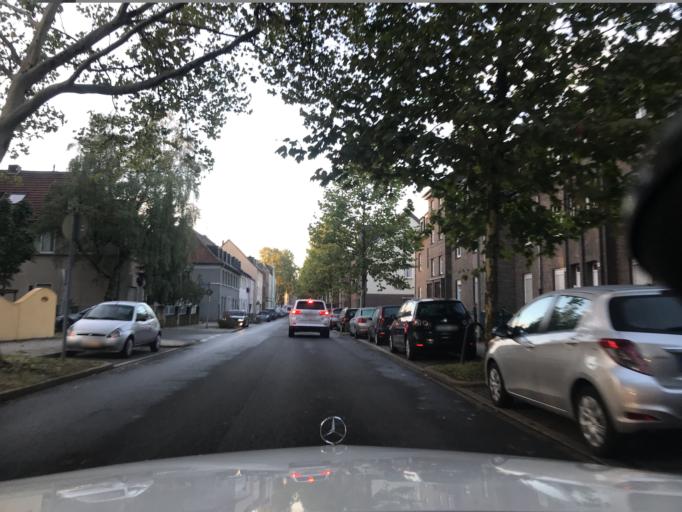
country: DE
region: North Rhine-Westphalia
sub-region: Regierungsbezirk Dusseldorf
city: Oberhausen
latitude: 51.4797
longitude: 6.8274
